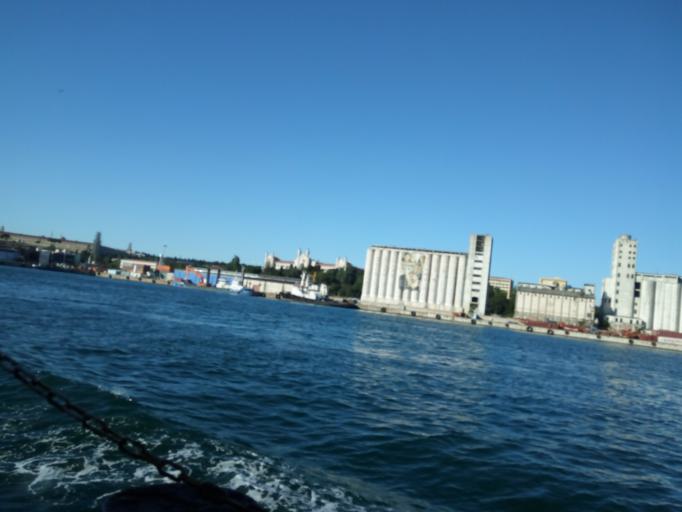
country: TR
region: Istanbul
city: UEskuedar
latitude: 40.9973
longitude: 29.0149
